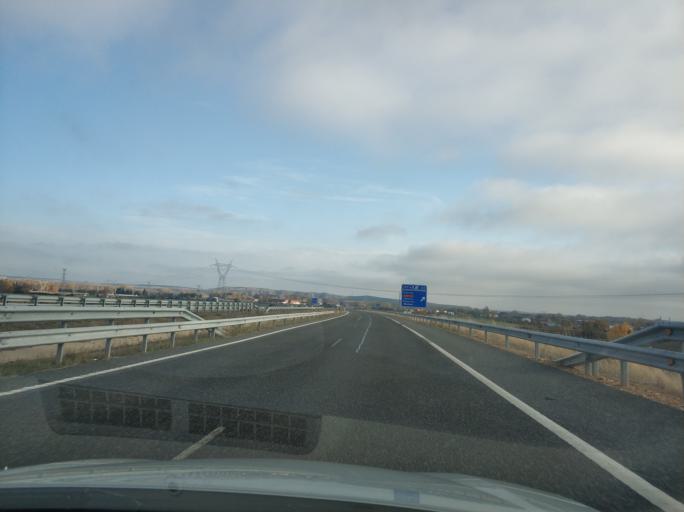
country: ES
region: Castille and Leon
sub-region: Provincia de Leon
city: Villaturiel
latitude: 42.5571
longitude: -5.4707
